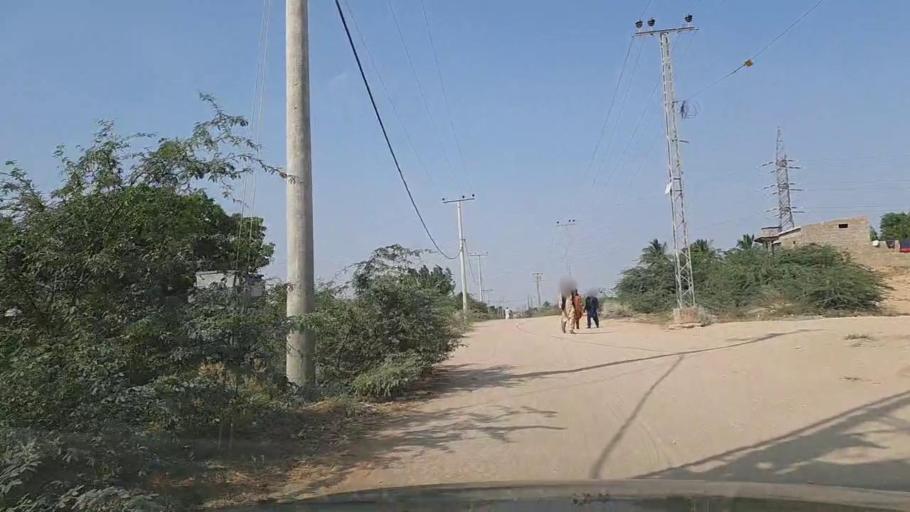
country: PK
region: Sindh
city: Gharo
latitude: 24.7470
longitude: 67.5826
